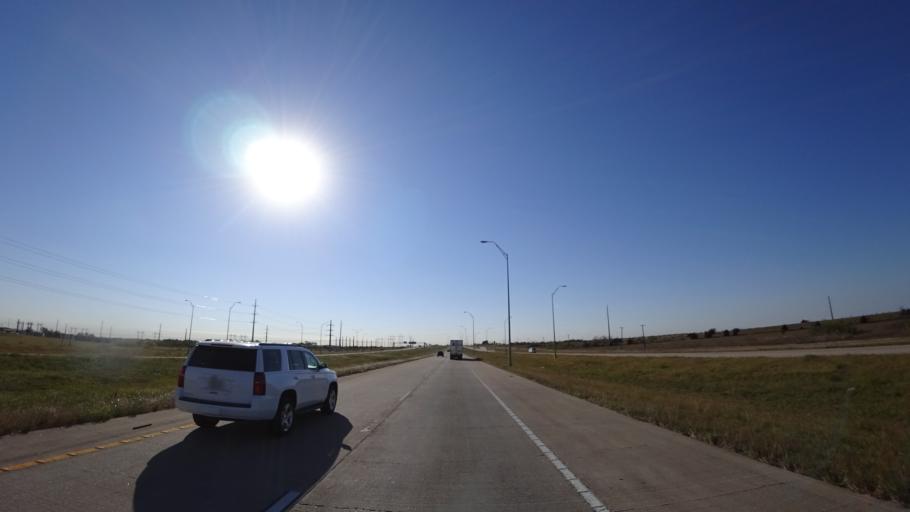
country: US
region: Texas
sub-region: Travis County
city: Pflugerville
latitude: 30.4131
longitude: -97.5855
